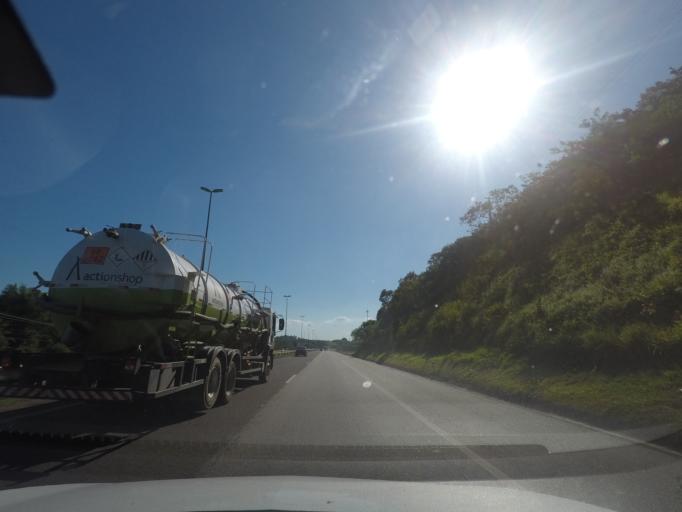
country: BR
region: Rio de Janeiro
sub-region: Guapimirim
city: Guapimirim
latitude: -22.6477
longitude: -43.0725
